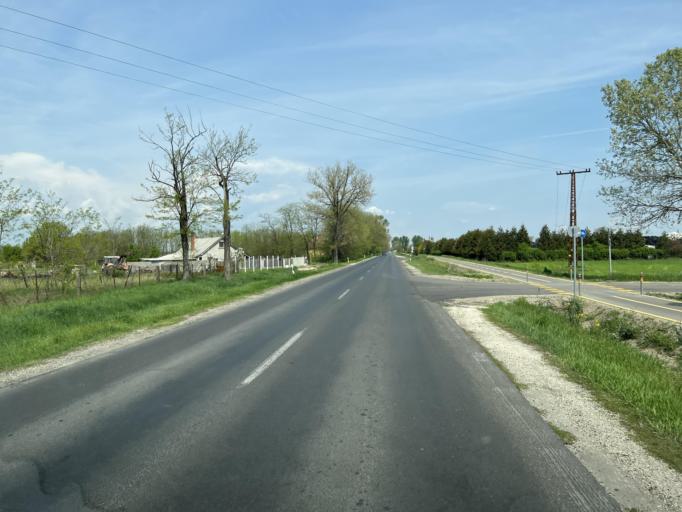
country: HU
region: Pest
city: Cegled
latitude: 47.1328
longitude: 19.7878
